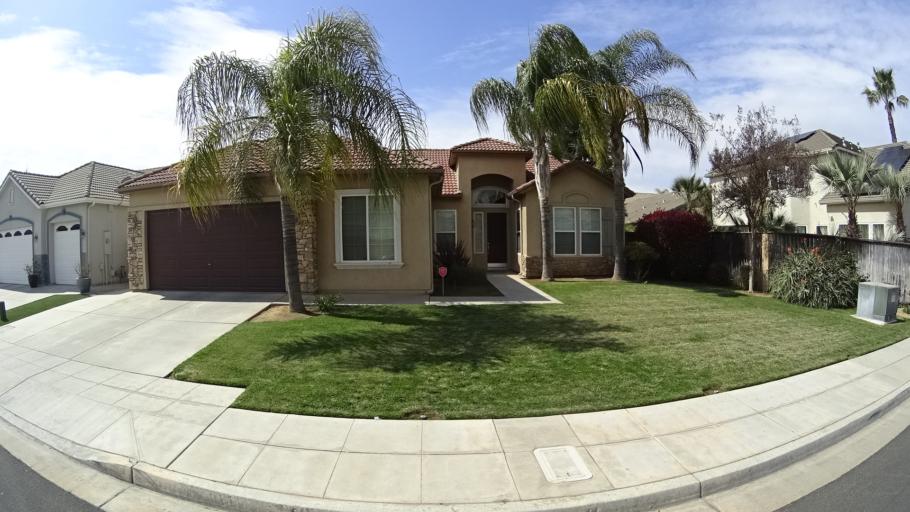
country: US
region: California
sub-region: Fresno County
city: Biola
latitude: 36.8414
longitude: -119.8946
